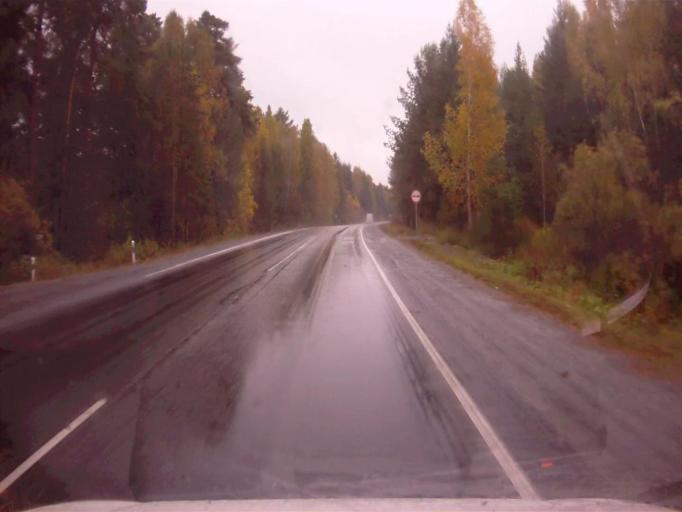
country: RU
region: Chelyabinsk
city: Tayginka
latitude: 55.5571
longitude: 60.6463
